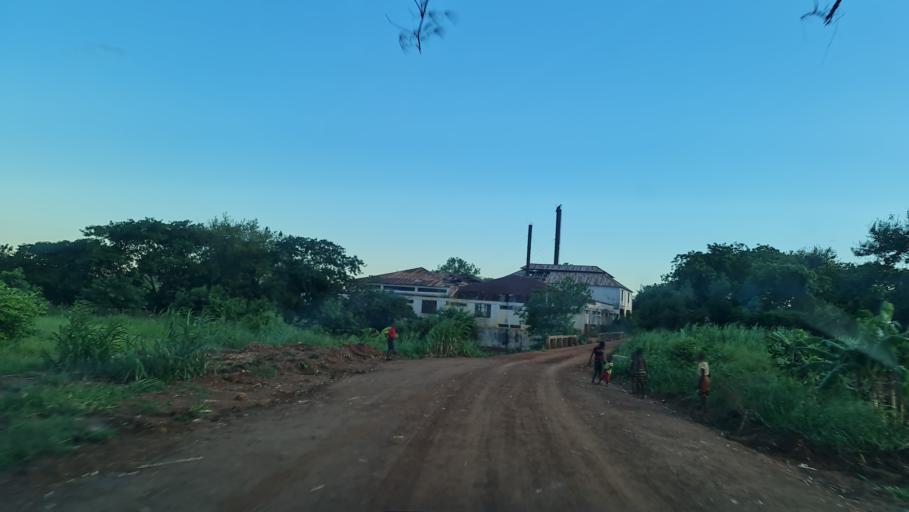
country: MZ
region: Nampula
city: Ilha de Mocambique
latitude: -14.9849
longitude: 40.0950
